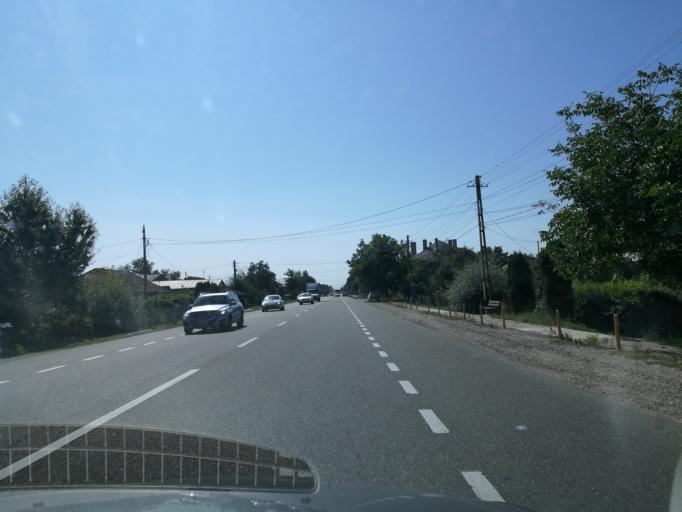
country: RO
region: Bacau
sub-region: Comuna Filipesti
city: Filipesti
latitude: 46.7453
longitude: 26.8847
